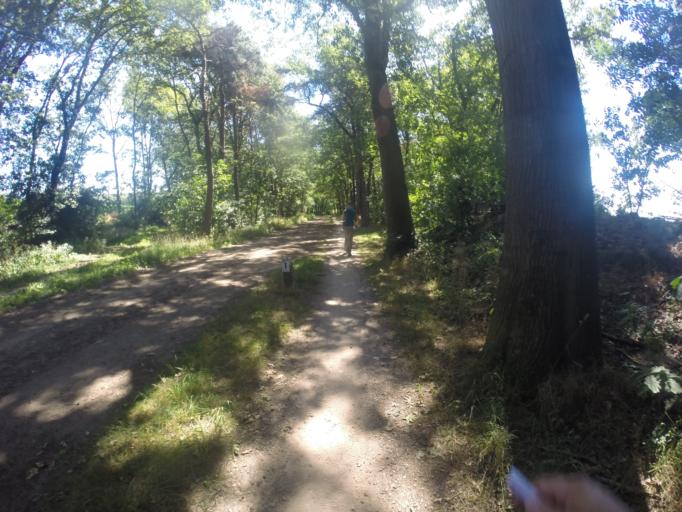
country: NL
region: Gelderland
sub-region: Gemeente Lochem
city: Barchem
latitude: 52.1309
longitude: 6.4264
